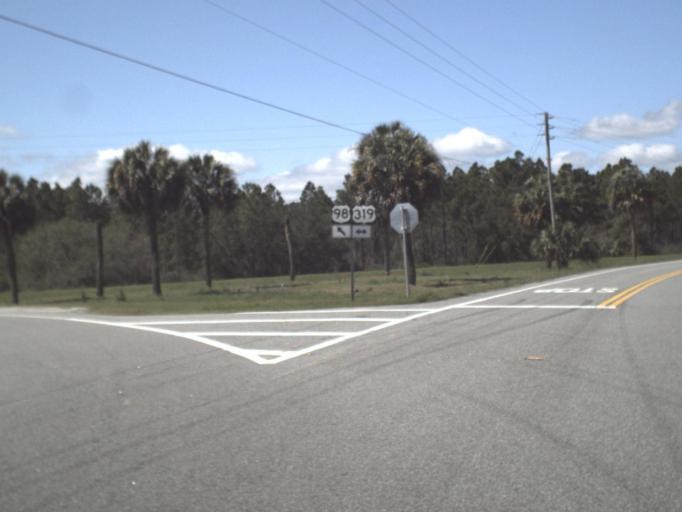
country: US
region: Florida
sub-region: Franklin County
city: Carrabelle
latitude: 29.9185
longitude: -84.5196
